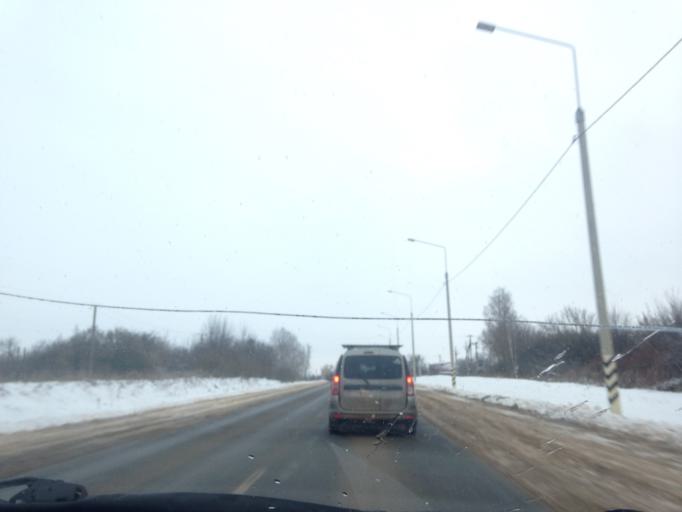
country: RU
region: Tula
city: Shchekino
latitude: 53.9823
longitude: 37.5027
